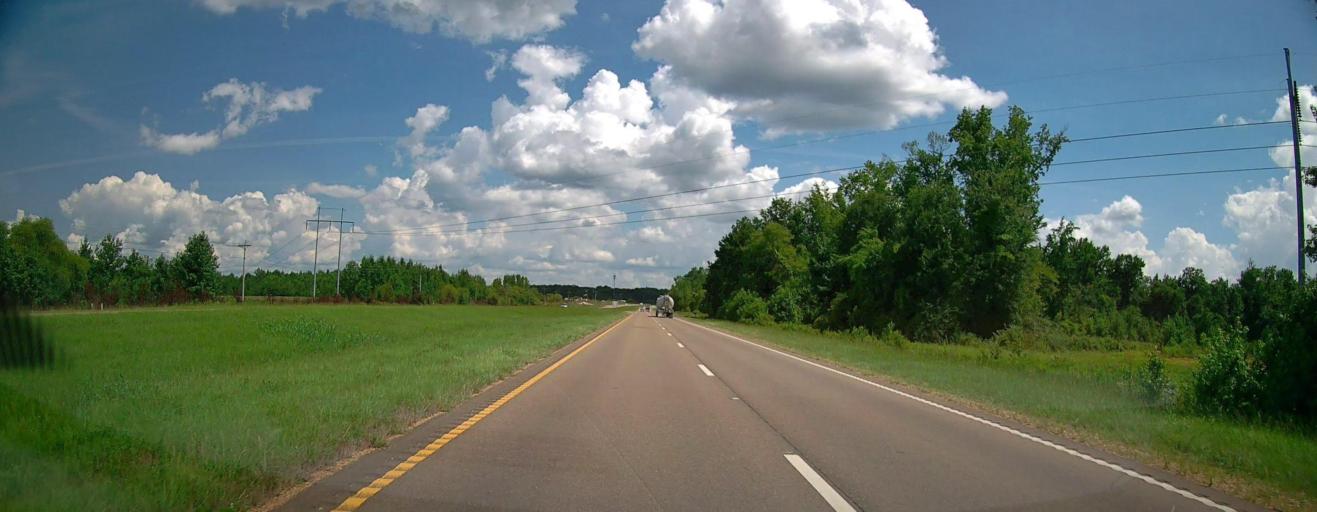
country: US
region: Mississippi
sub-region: Lowndes County
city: Columbus Air Force Base
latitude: 33.6623
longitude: -88.4228
